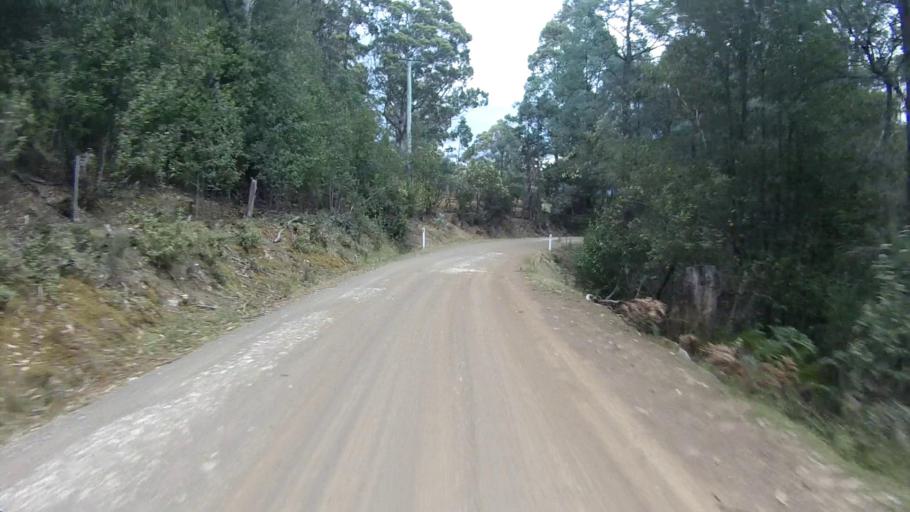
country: AU
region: Tasmania
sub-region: Huon Valley
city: Huonville
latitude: -42.9554
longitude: 147.0477
